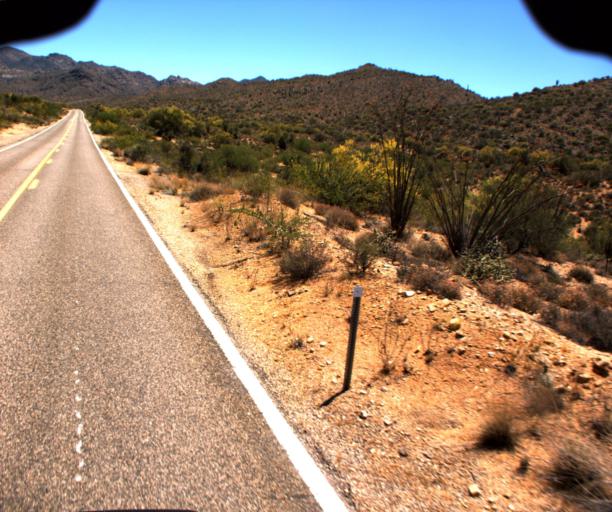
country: US
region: Arizona
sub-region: Yavapai County
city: Bagdad
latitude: 34.4686
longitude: -113.0493
